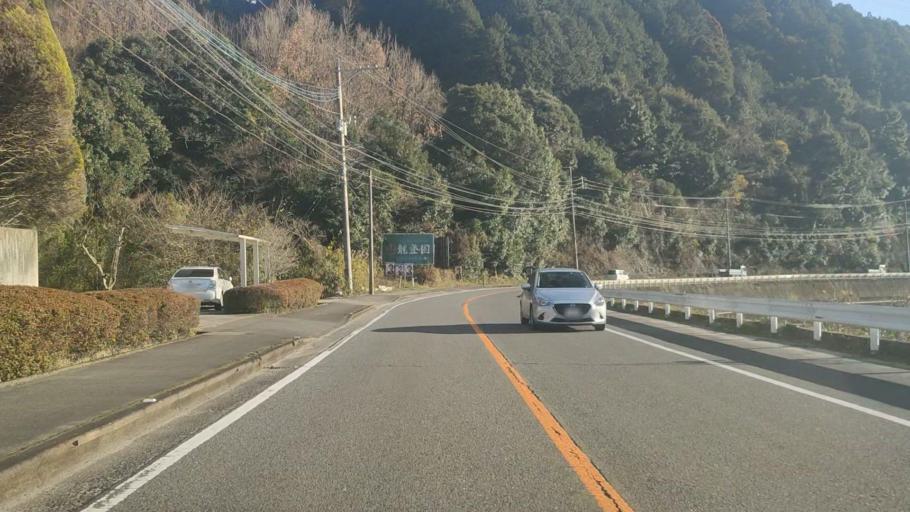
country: JP
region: Saga Prefecture
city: Saga-shi
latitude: 33.3494
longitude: 130.2491
